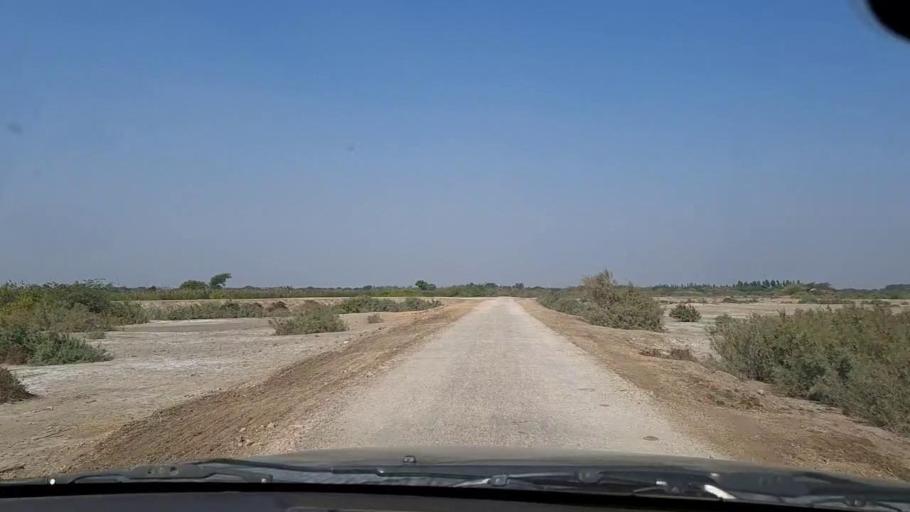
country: PK
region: Sindh
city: Chuhar Jamali
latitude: 24.4348
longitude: 67.7994
